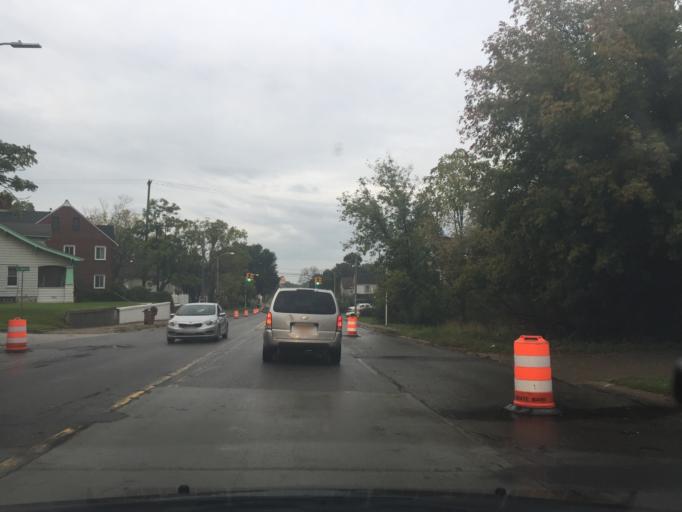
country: US
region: Michigan
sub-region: Oakland County
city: Pontiac
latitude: 42.6473
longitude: -83.2878
